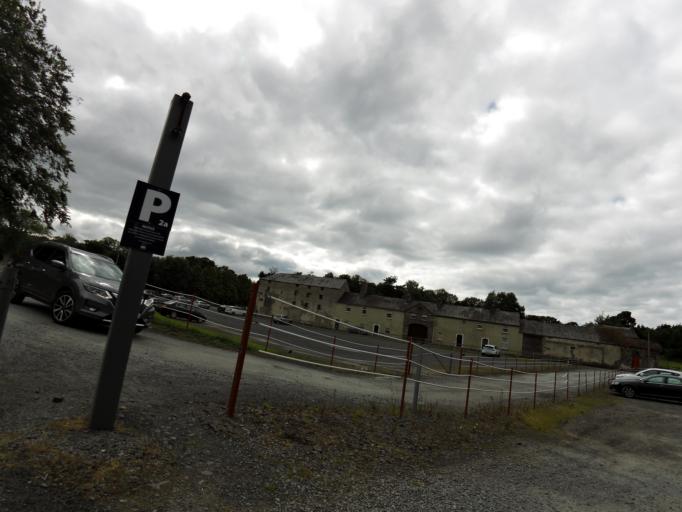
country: IE
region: Connaught
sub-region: Maigh Eo
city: Westport
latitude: 53.8052
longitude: -9.5382
